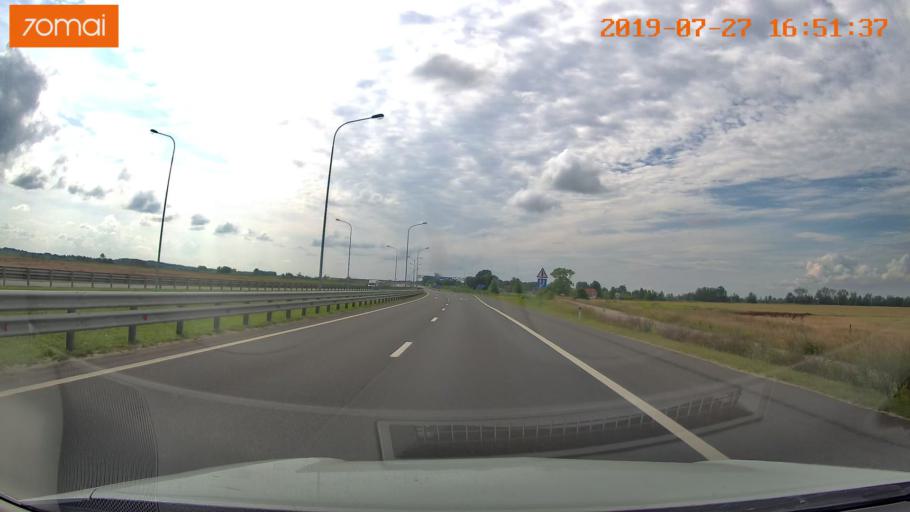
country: RU
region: Kaliningrad
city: Gvardeysk
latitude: 54.6835
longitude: 20.8818
